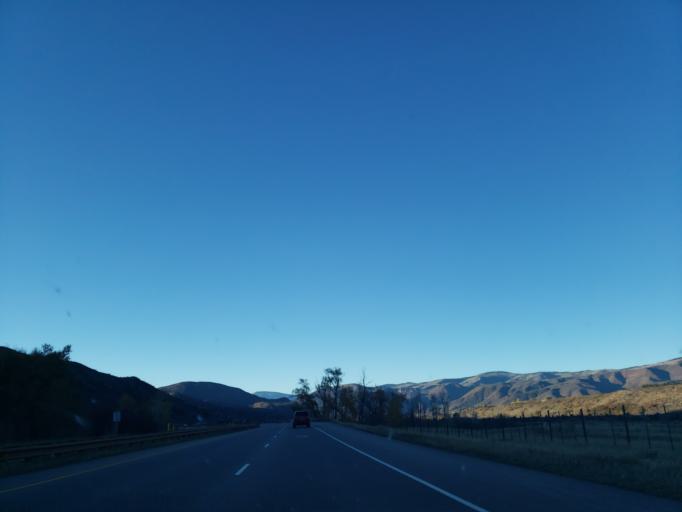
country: US
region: Colorado
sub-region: Pitkin County
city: Aspen
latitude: 39.2330
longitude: -106.8709
